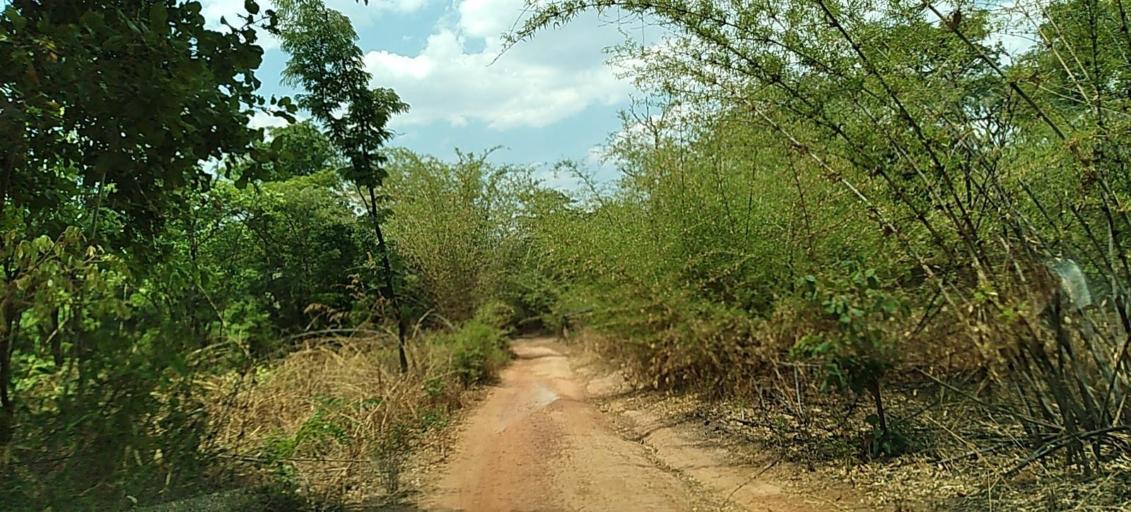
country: ZM
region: Copperbelt
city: Chililabombwe
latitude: -12.4753
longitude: 27.6498
